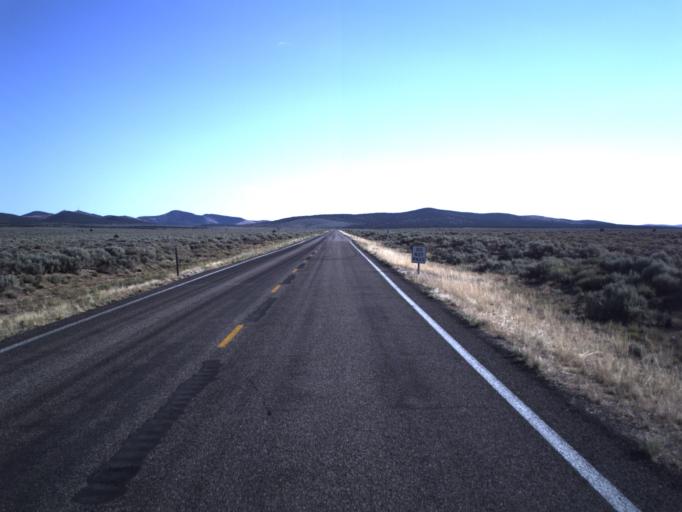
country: US
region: Utah
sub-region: Iron County
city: Enoch
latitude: 37.9855
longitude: -113.0022
